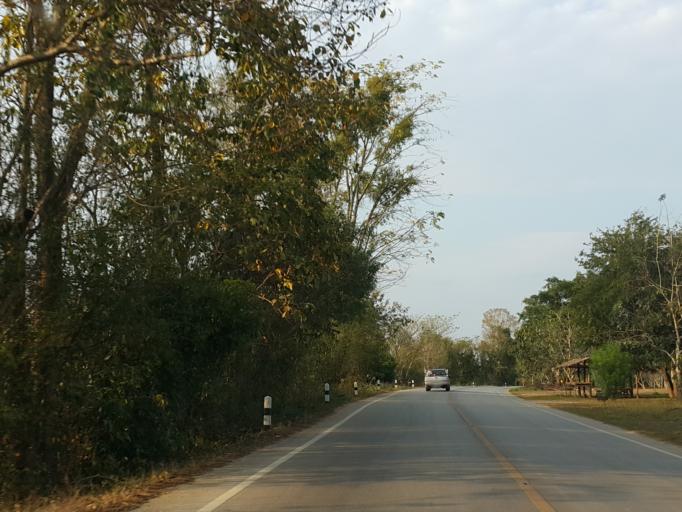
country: TH
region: Lampang
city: Chae Hom
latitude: 18.5230
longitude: 99.4769
